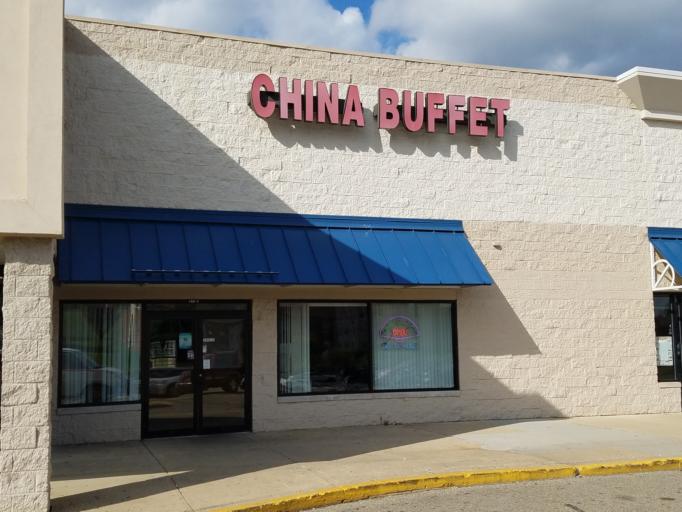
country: US
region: Ohio
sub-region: Knox County
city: Mount Vernon
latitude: 40.4031
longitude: -82.4484
